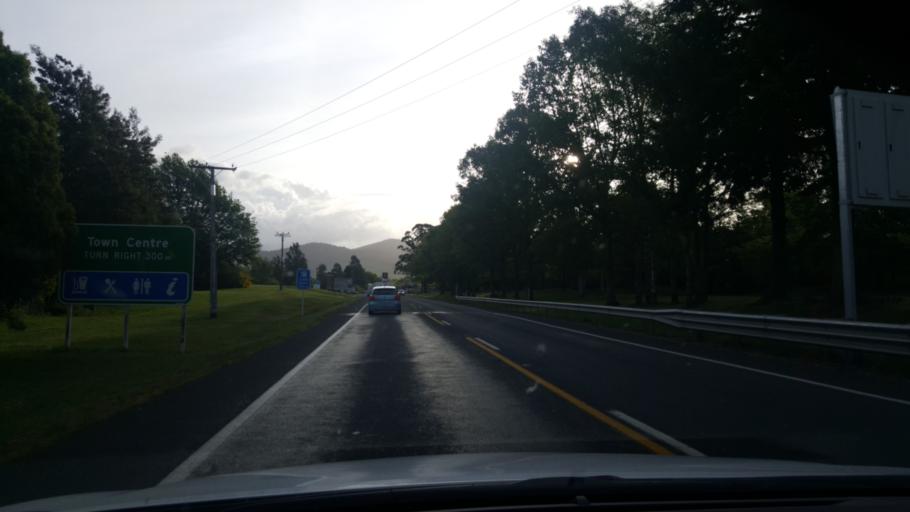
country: NZ
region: Waikato
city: Turangi
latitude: -38.9890
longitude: 175.8144
